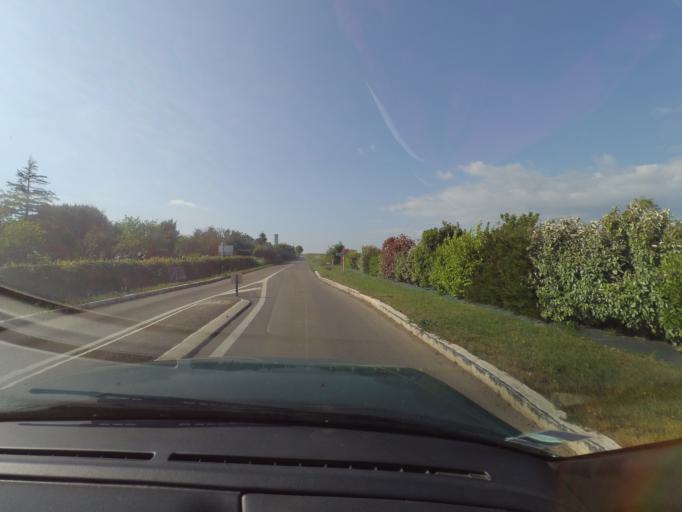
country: FR
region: Pays de la Loire
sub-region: Departement de la Vendee
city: Angles
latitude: 46.4085
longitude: -1.3840
